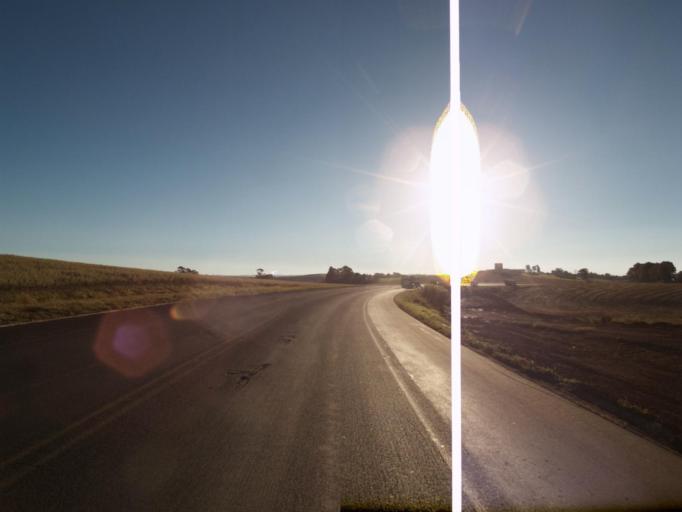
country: BR
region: Santa Catarina
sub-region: Chapeco
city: Chapeco
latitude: -26.8793
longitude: -52.9497
